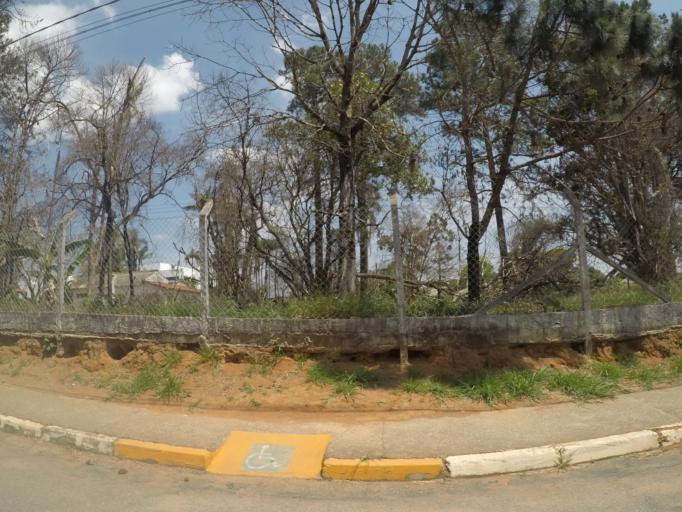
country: BR
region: Sao Paulo
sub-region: Itupeva
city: Itupeva
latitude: -23.2448
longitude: -47.0572
